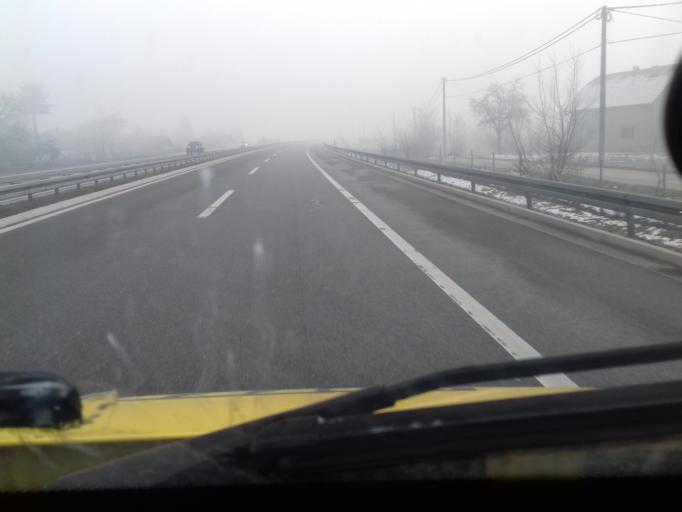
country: BA
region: Federation of Bosnia and Herzegovina
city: Ilijas
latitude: 43.9415
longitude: 18.2668
